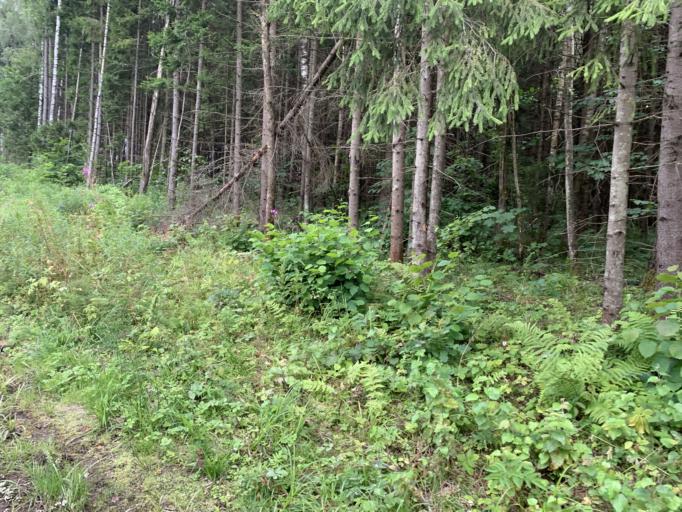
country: RU
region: Moskovskaya
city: Podosinki
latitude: 56.1823
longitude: 37.5760
